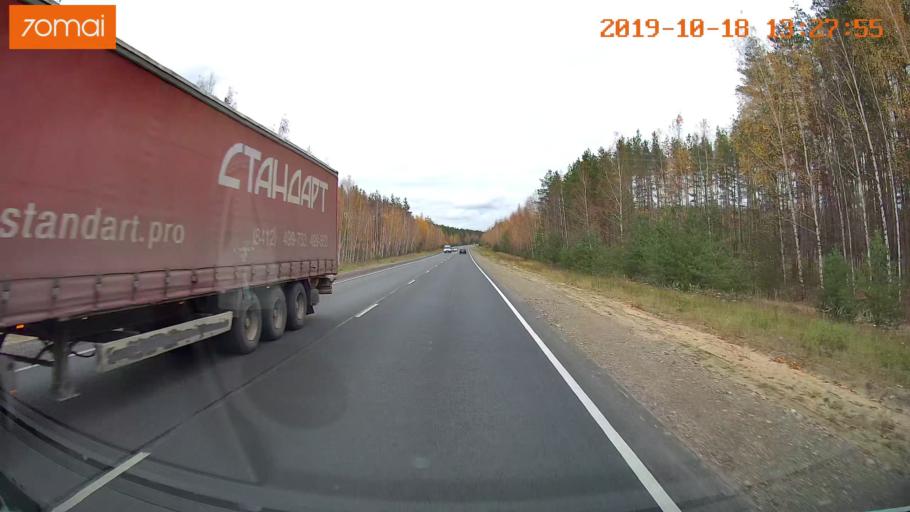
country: RU
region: Rjazan
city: Solotcha
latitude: 54.7712
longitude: 39.8599
